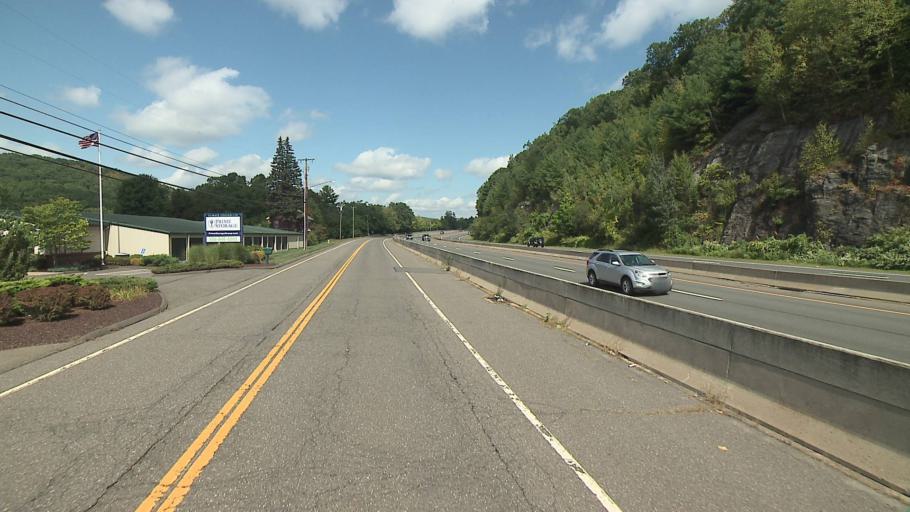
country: US
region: Connecticut
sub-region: New Haven County
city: Seymour
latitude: 41.4129
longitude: -73.0709
